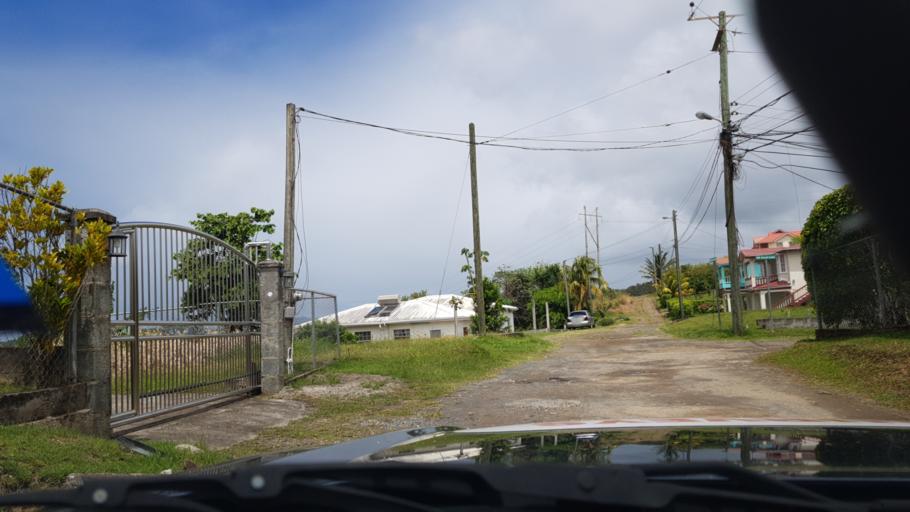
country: LC
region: Anse-la-Raye
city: Anse La Raye
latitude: 13.9462
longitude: -61.0321
